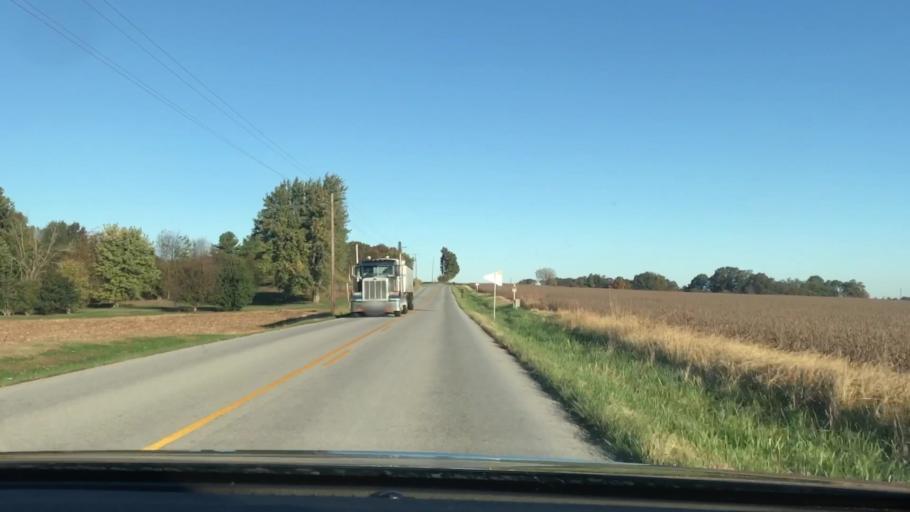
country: US
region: Kentucky
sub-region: Simpson County
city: Franklin
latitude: 36.7777
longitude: -86.6191
